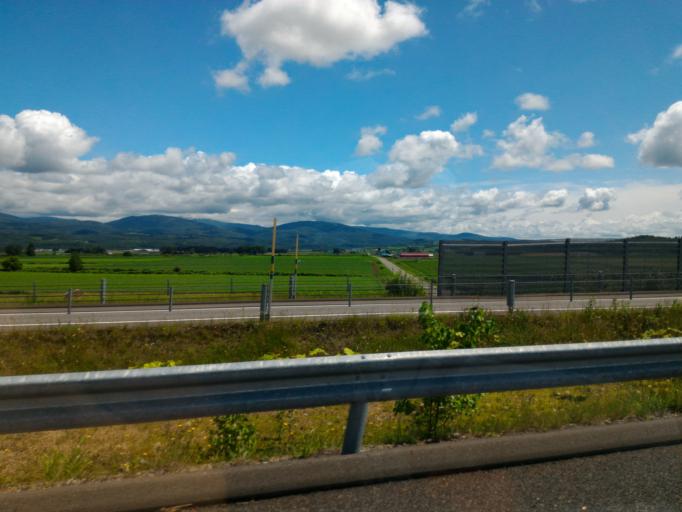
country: JP
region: Hokkaido
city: Nayoro
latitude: 44.4395
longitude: 142.3700
